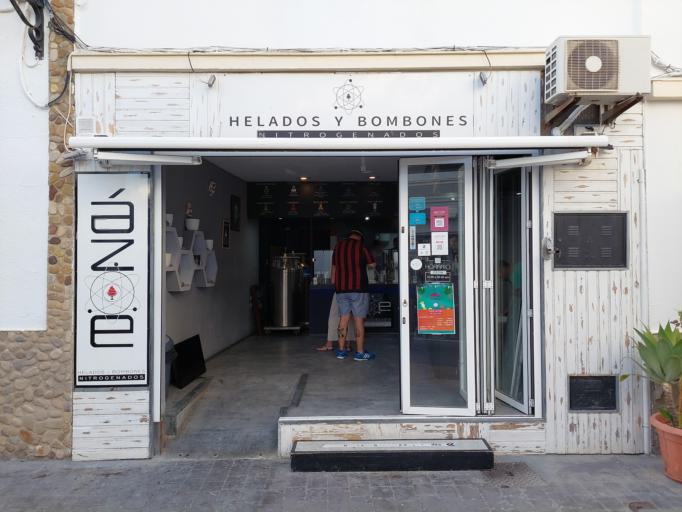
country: ES
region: Andalusia
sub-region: Provincia de Cadiz
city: Zahara de los Atunes
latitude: 36.1365
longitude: -5.8473
